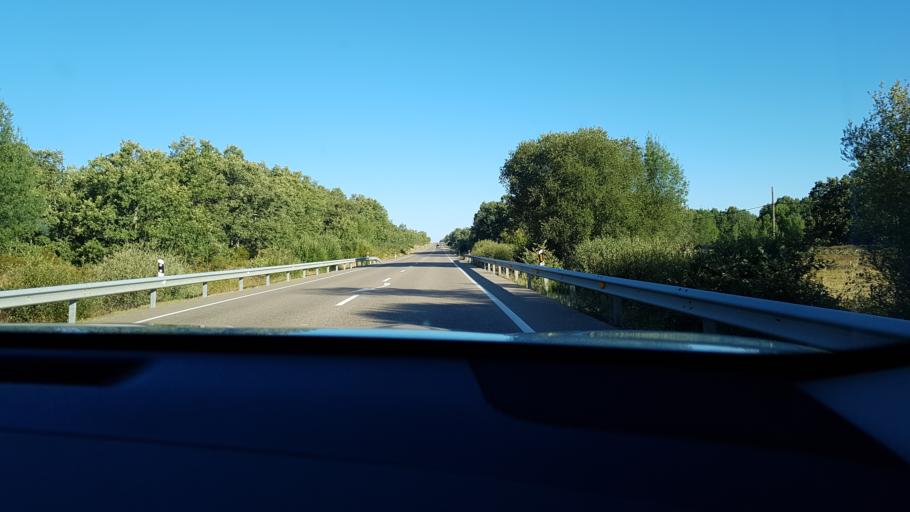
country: ES
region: Castille and Leon
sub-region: Provincia de Zamora
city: Samir de los Canos
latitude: 41.6715
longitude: -6.2326
